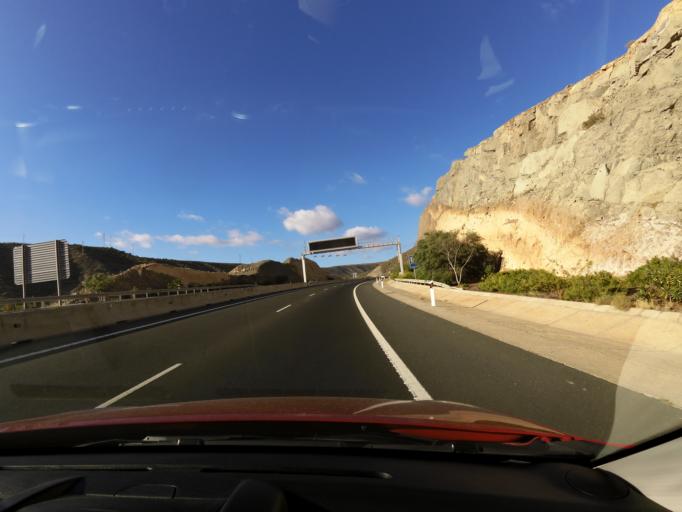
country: ES
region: Canary Islands
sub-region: Provincia de Las Palmas
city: Puerto Rico
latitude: 27.7753
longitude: -15.6763
